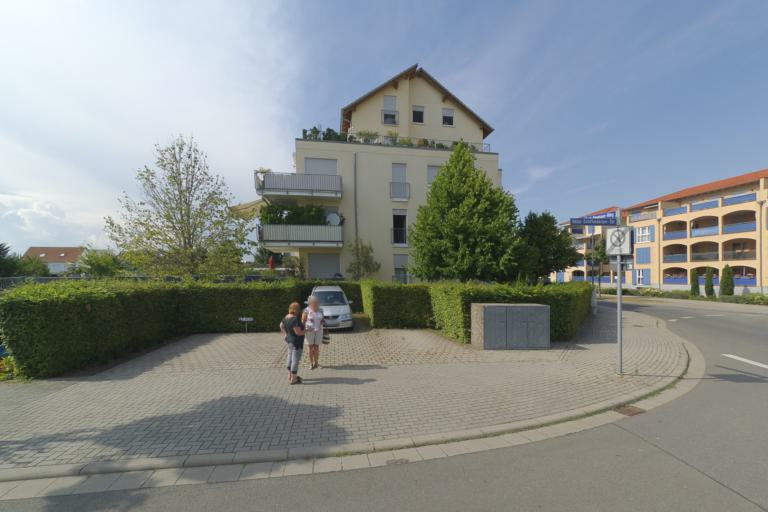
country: DE
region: Rheinland-Pfalz
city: Frankenthal
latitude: 49.5062
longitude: 8.3848
